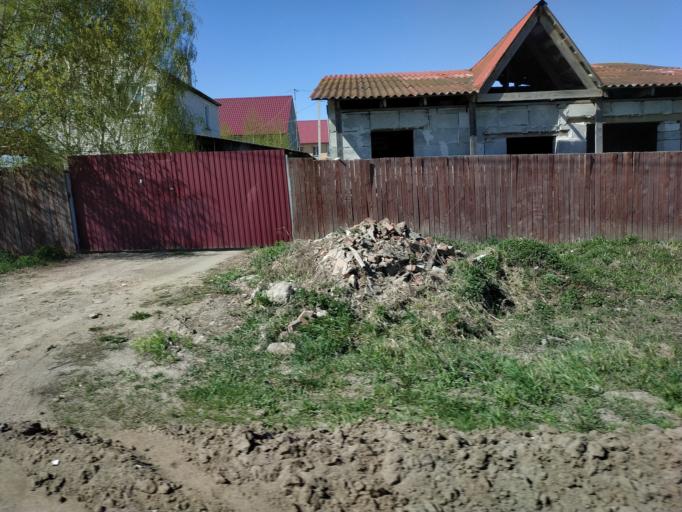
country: RU
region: Moskovskaya
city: Malyshevo
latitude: 55.4575
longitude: 38.3753
